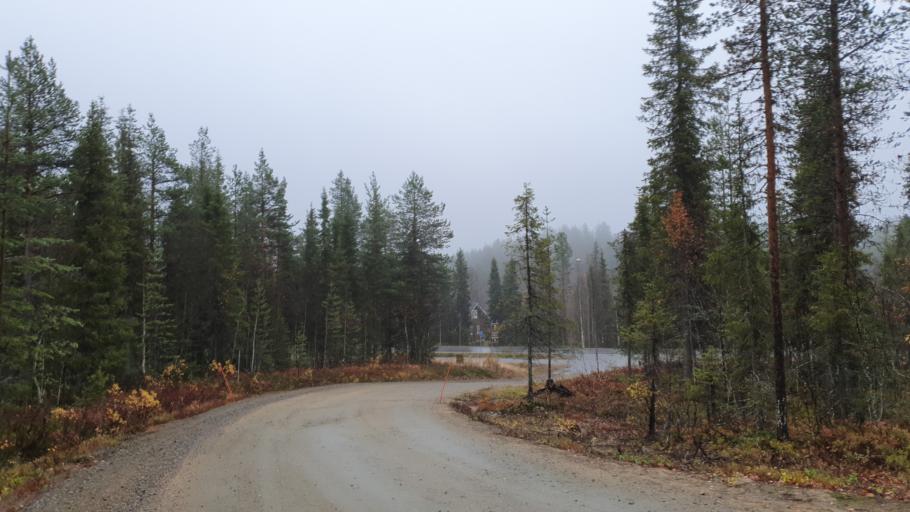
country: FI
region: Lapland
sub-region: Tunturi-Lappi
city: Kolari
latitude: 67.6028
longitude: 24.1314
